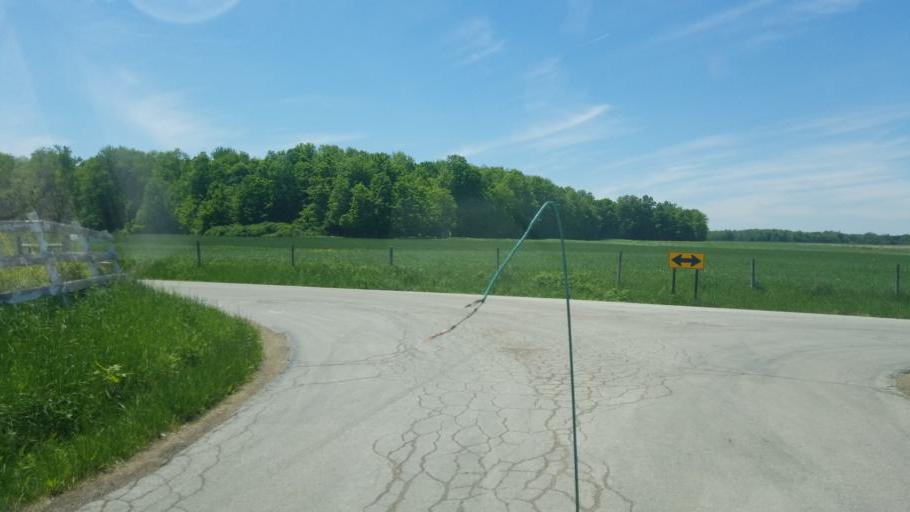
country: US
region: Ohio
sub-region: Huron County
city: Greenwich
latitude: 40.9680
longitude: -82.4315
